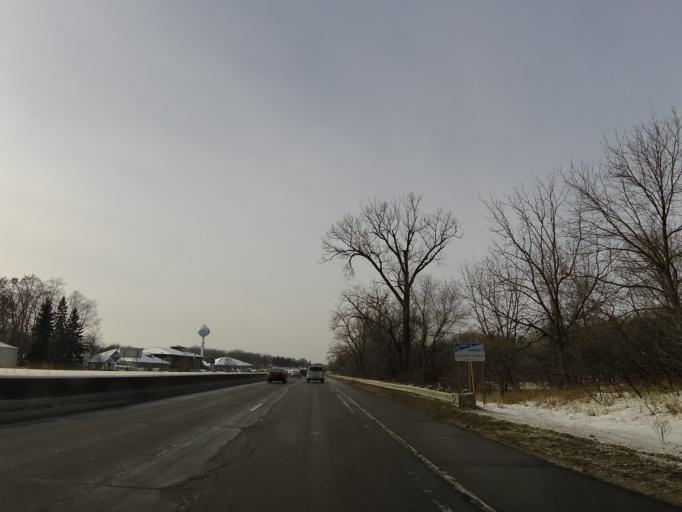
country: US
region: Minnesota
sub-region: Hennepin County
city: Deephaven
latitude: 44.9100
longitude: -93.5273
